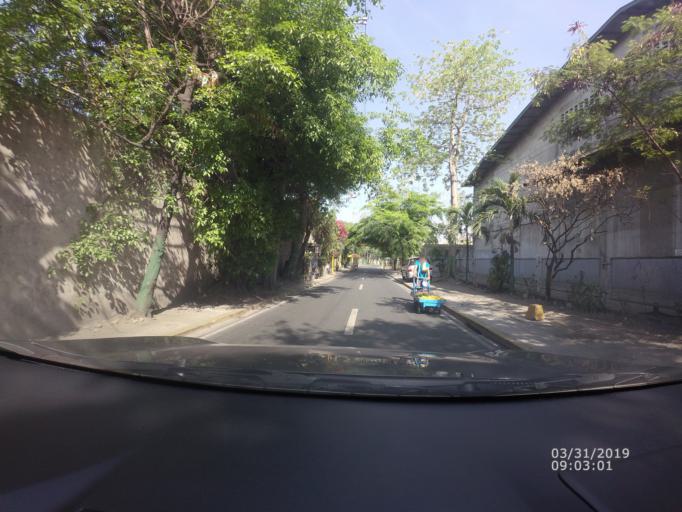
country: PH
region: Metro Manila
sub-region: Mandaluyong
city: Mandaluyong City
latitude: 14.5783
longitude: 121.0215
